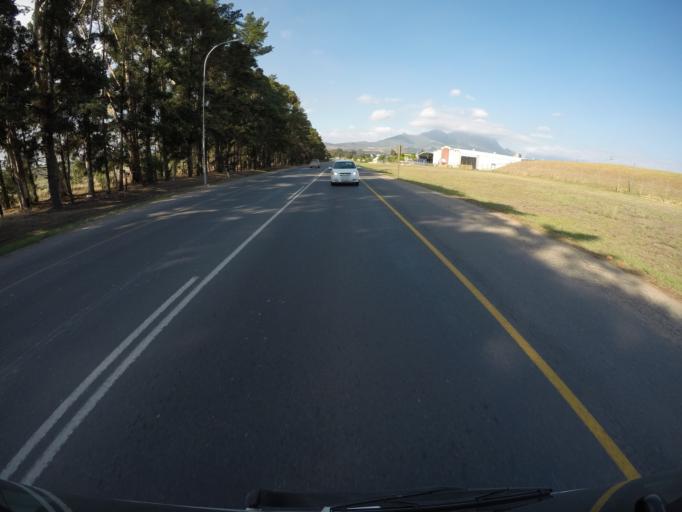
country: ZA
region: Western Cape
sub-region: Cape Winelands District Municipality
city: Stellenbosch
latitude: -33.8773
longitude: 18.8065
